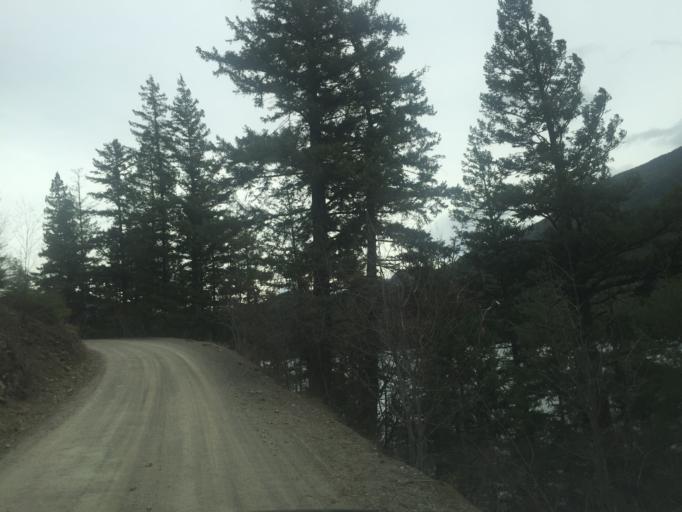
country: CA
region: British Columbia
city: Chase
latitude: 51.4351
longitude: -120.1365
